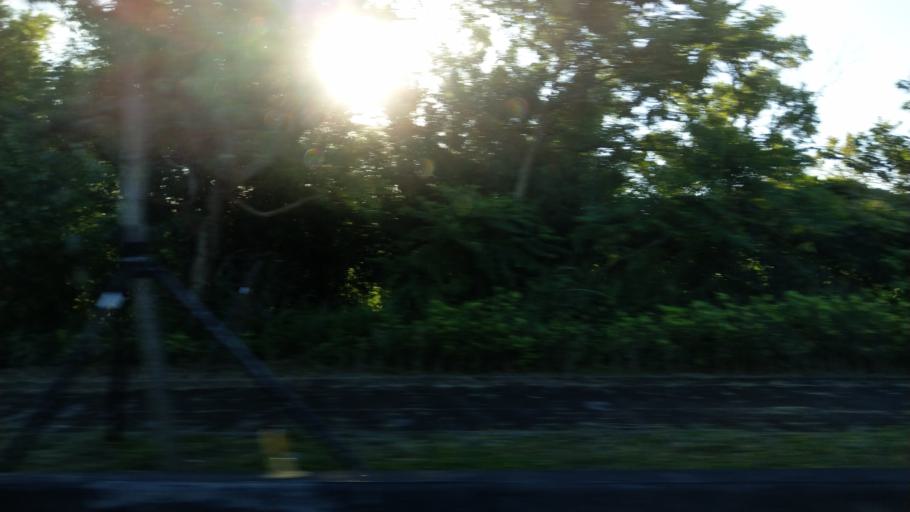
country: TW
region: Taiwan
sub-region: Miaoli
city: Miaoli
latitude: 24.5396
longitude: 120.7961
